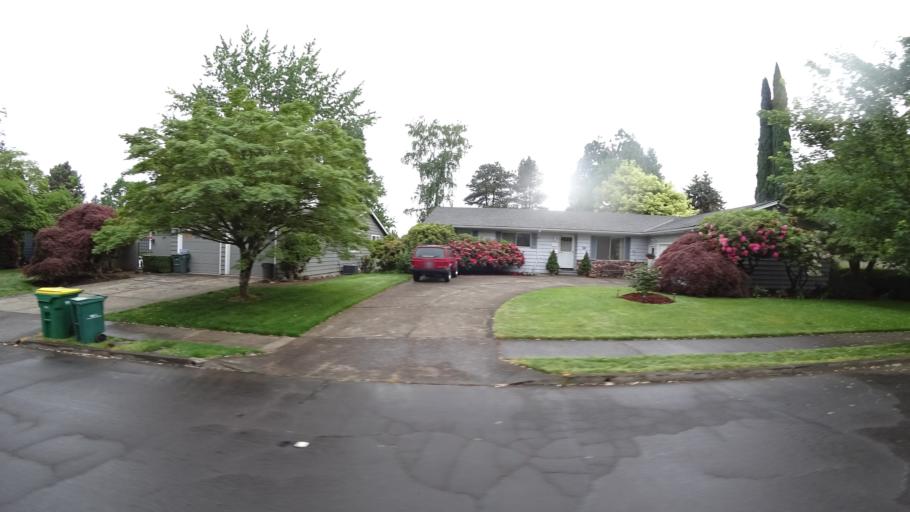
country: US
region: Oregon
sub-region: Washington County
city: Raleigh Hills
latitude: 45.4745
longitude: -122.7727
